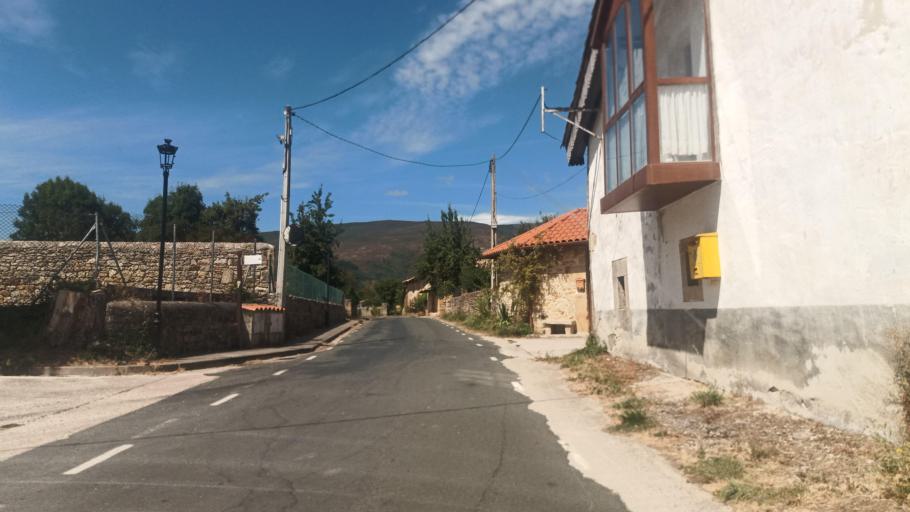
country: ES
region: Castille and Leon
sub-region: Provincia de Burgos
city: Espinosa de los Monteros
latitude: 43.0401
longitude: -3.6662
